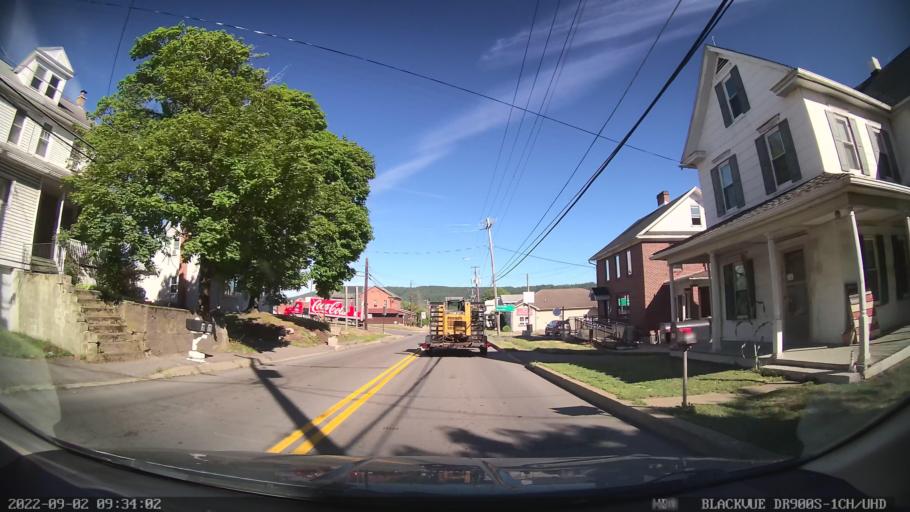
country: US
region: Pennsylvania
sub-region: Northumberland County
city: Elysburg
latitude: 40.8626
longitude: -76.5502
